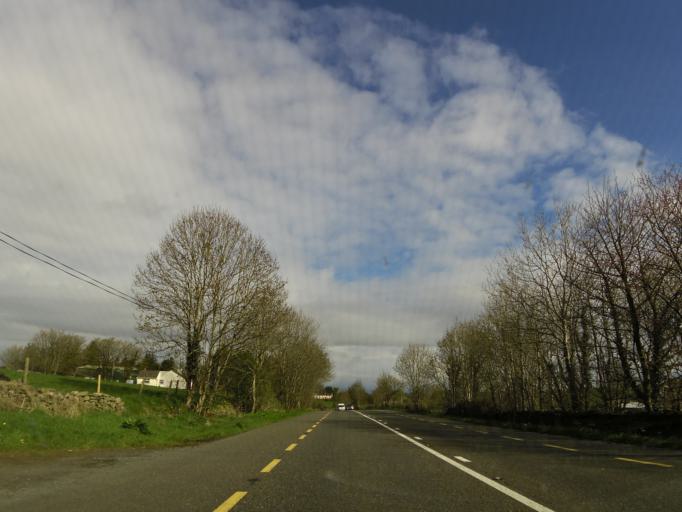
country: IE
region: Connaught
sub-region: Sligo
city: Tobercurry
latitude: 53.9322
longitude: -8.7860
